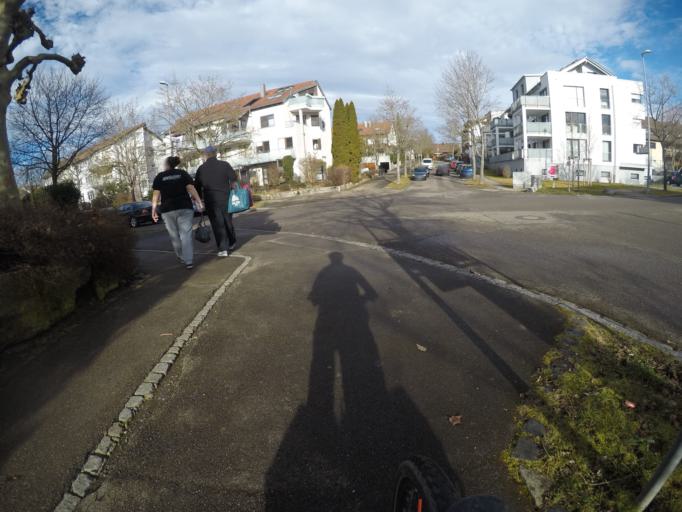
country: DE
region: Baden-Wuerttemberg
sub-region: Regierungsbezirk Stuttgart
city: Gartringen
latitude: 48.6461
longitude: 8.8986
